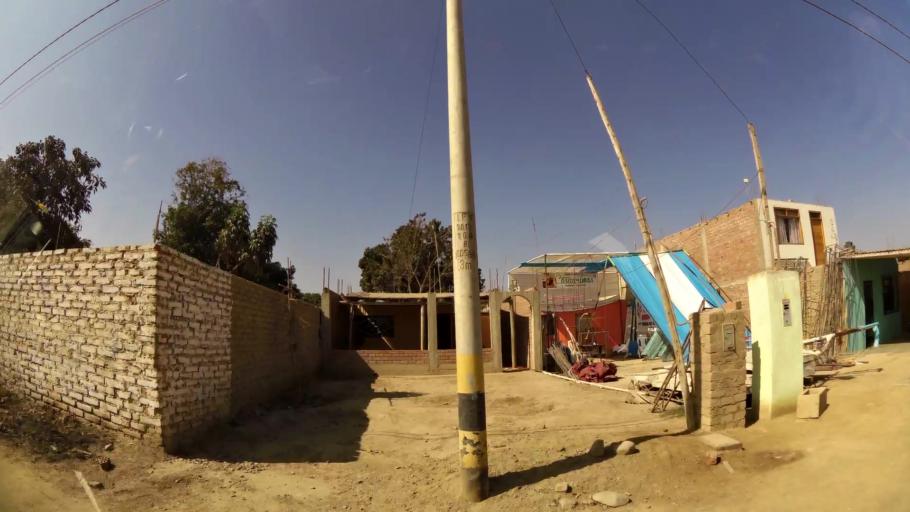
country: PE
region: Ica
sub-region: Provincia de Chincha
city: Sunampe
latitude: -13.4229
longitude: -76.1679
